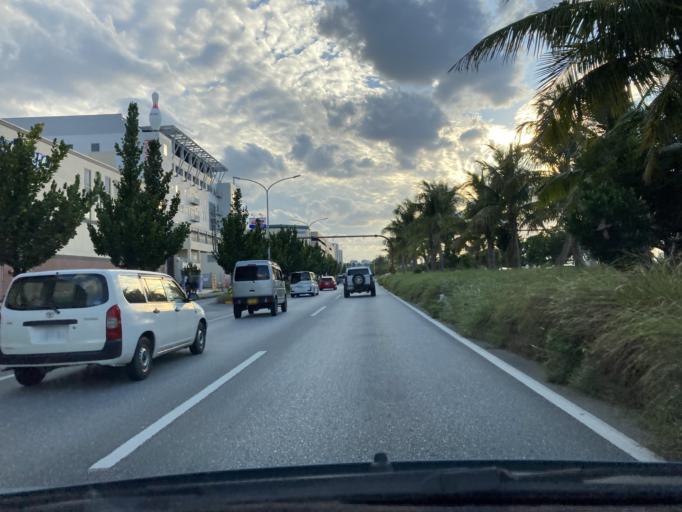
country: JP
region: Okinawa
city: Ginowan
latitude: 26.2772
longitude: 127.7317
